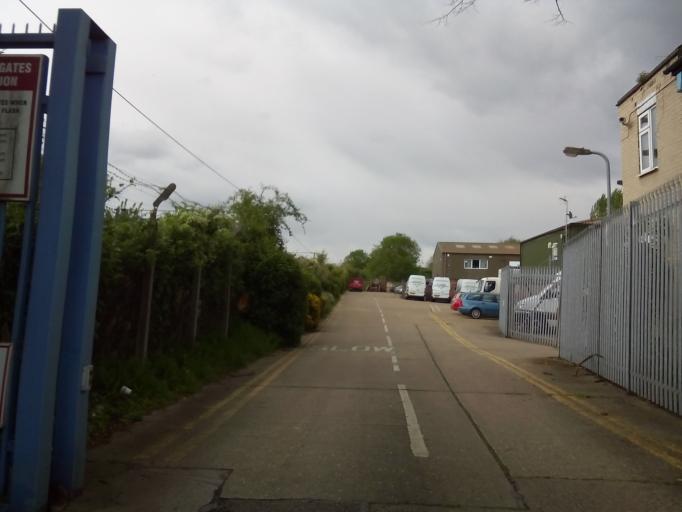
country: GB
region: England
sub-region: Cambridgeshire
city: Cambridge
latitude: 52.2102
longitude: 0.1494
